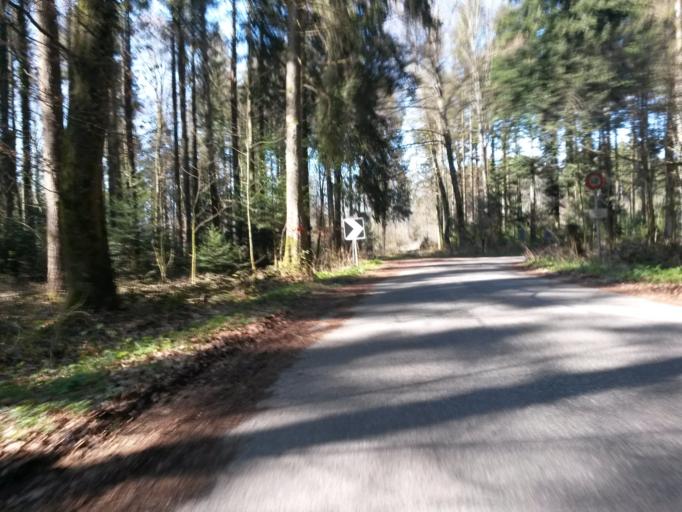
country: CH
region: Bern
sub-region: Emmental District
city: Koppigen
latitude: 47.1538
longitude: 7.6073
